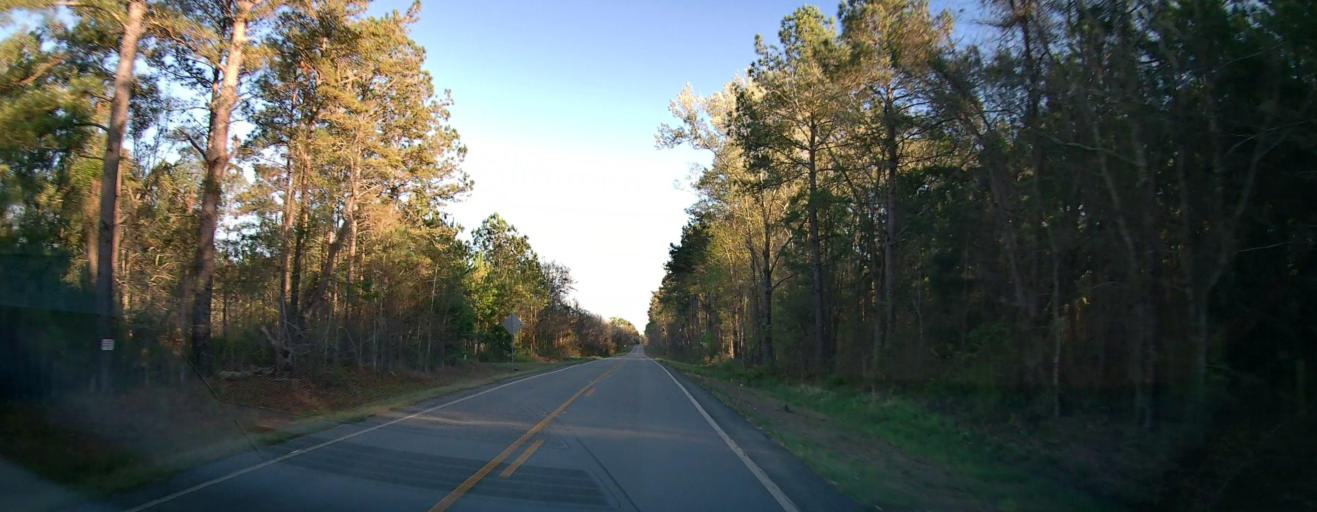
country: US
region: Georgia
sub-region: Wilcox County
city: Abbeville
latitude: 32.1095
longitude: -83.3156
